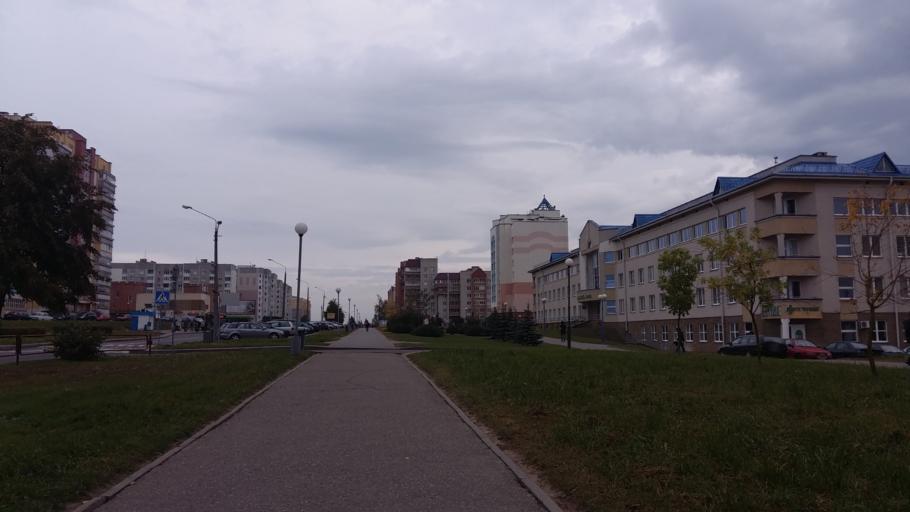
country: BY
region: Grodnenskaya
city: Hrodna
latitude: 53.7093
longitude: 23.8498
